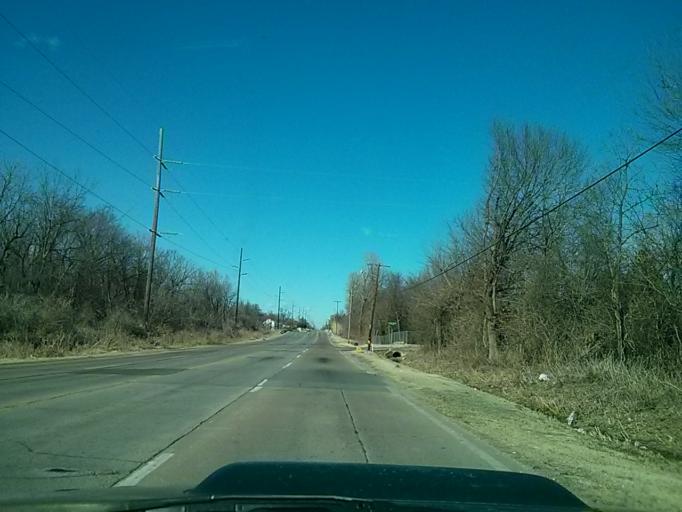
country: US
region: Oklahoma
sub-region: Tulsa County
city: Turley
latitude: 36.2127
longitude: -95.9582
